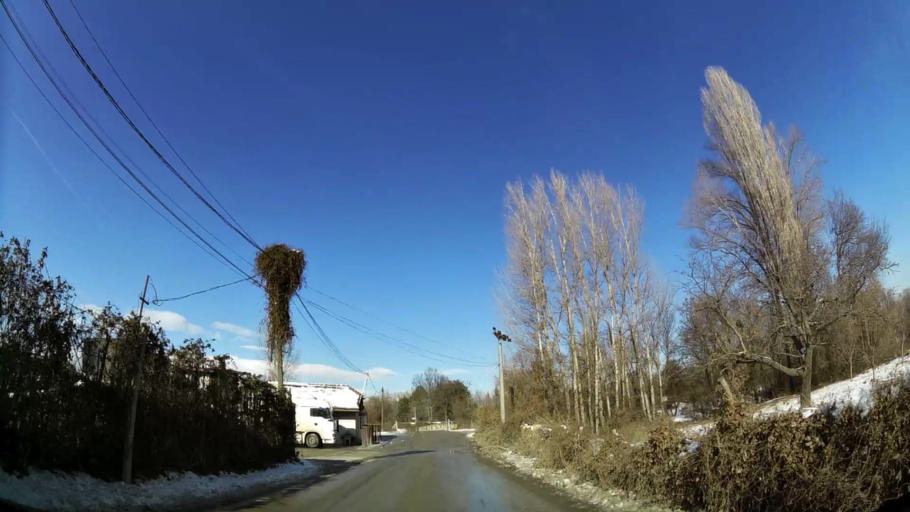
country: MK
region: Saraj
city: Saraj
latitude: 41.9982
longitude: 21.3425
